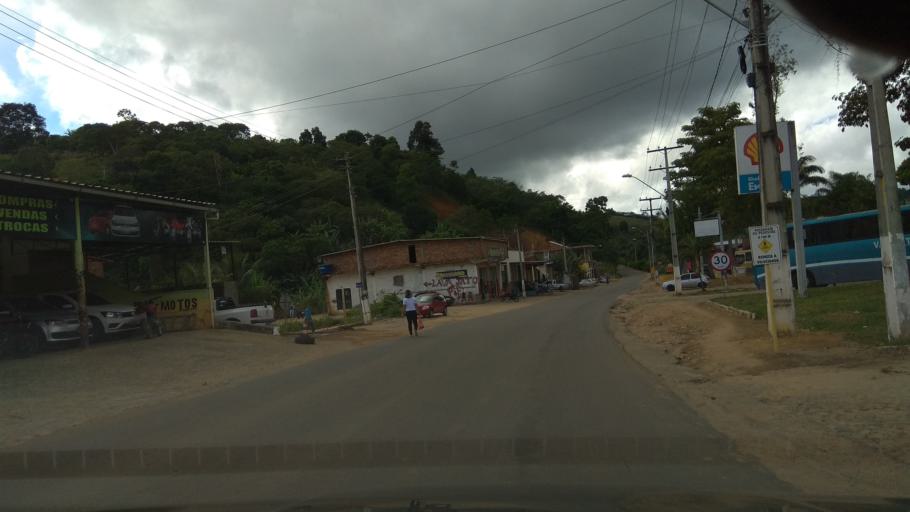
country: BR
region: Bahia
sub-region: Mutuipe
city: Mutuipe
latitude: -13.2519
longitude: -39.5690
